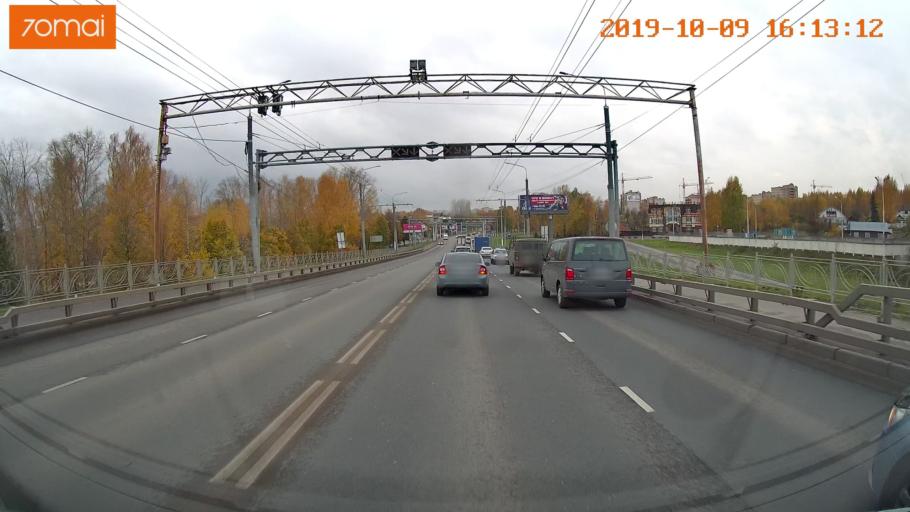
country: RU
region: Kostroma
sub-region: Kostromskoy Rayon
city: Kostroma
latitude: 57.7483
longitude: 40.9322
